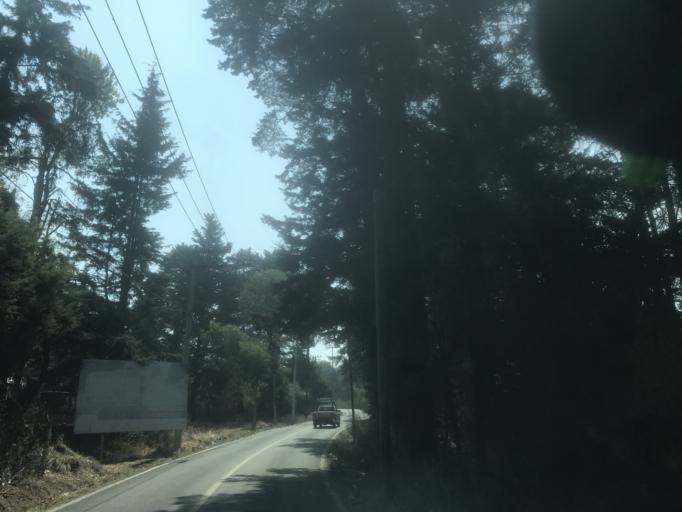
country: MX
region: Mexico
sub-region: Atlautla
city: San Juan Tepecoculco
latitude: 18.9982
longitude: -98.7737
